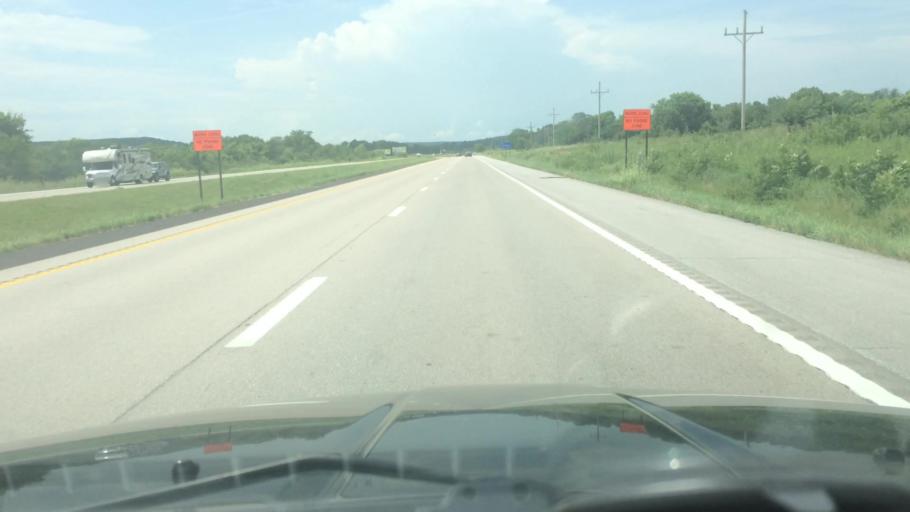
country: US
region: Missouri
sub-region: Polk County
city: Humansville
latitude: 37.8108
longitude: -93.6048
